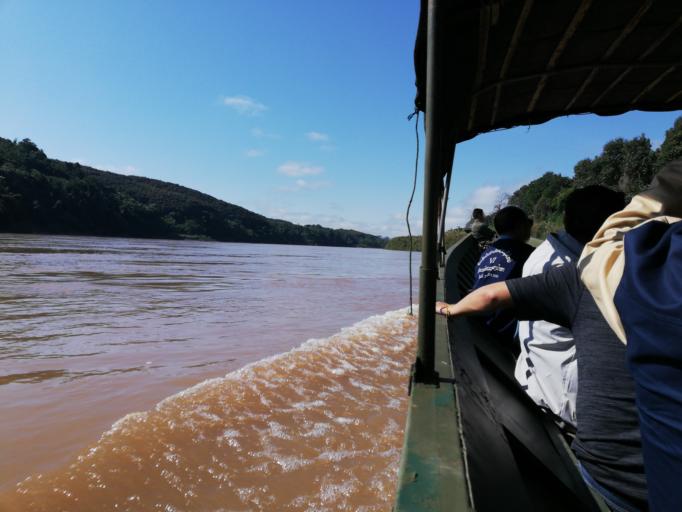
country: LA
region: Loungnamtha
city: Muang Long
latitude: 20.8948
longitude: 100.6186
